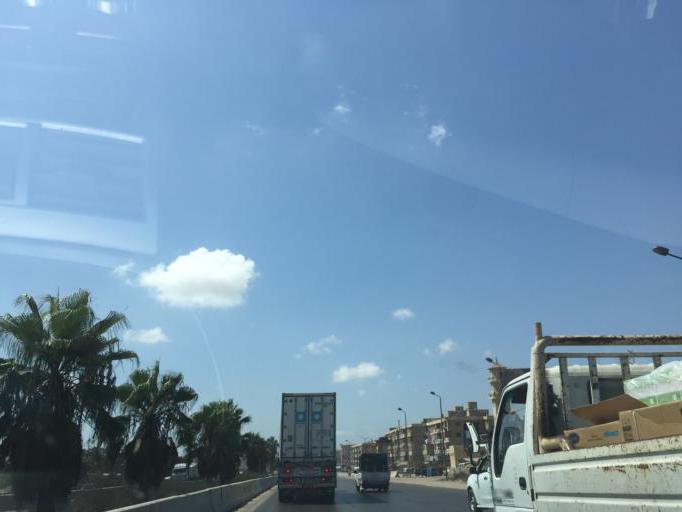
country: EG
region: Alexandria
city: Alexandria
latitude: 31.0067
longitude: 29.8034
